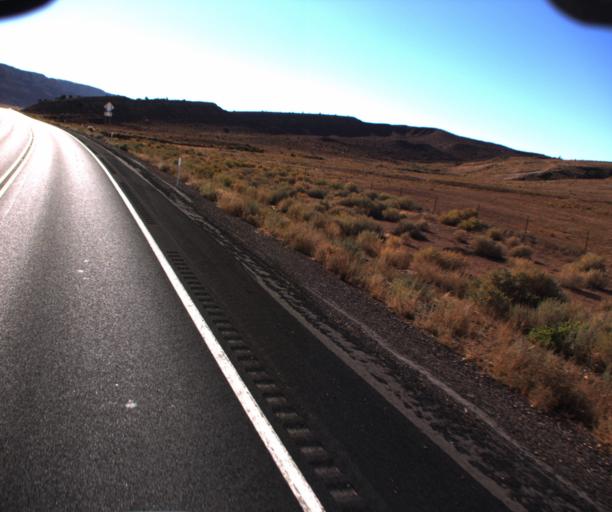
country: US
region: Arizona
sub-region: Coconino County
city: LeChee
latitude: 36.5193
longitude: -111.5967
